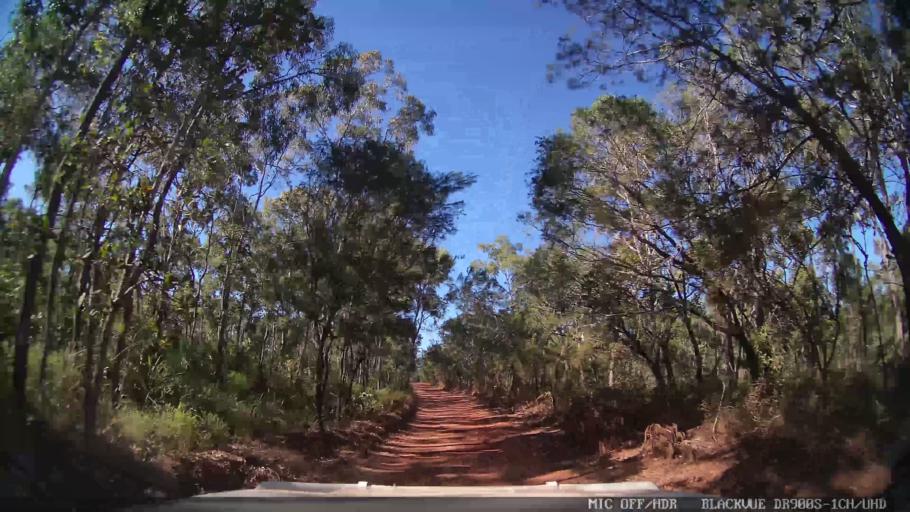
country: AU
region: Queensland
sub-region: Torres
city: Thursday Island
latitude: -11.4068
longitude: 142.4078
